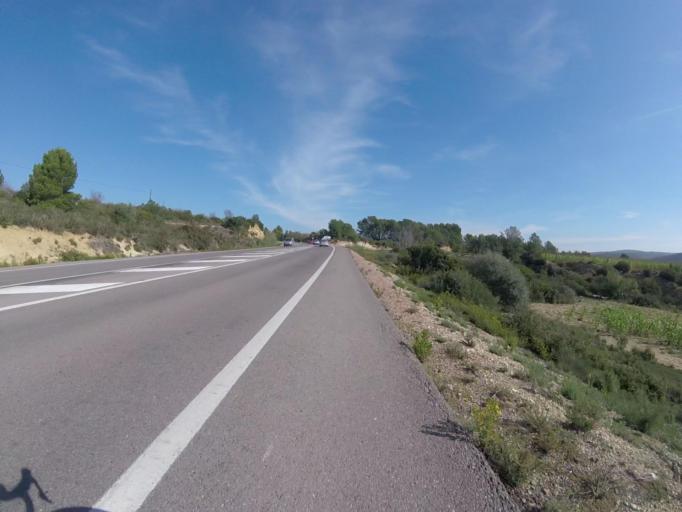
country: ES
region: Valencia
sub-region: Provincia de Castello
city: Cuevas de Vinroma
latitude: 40.2575
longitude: 0.0776
